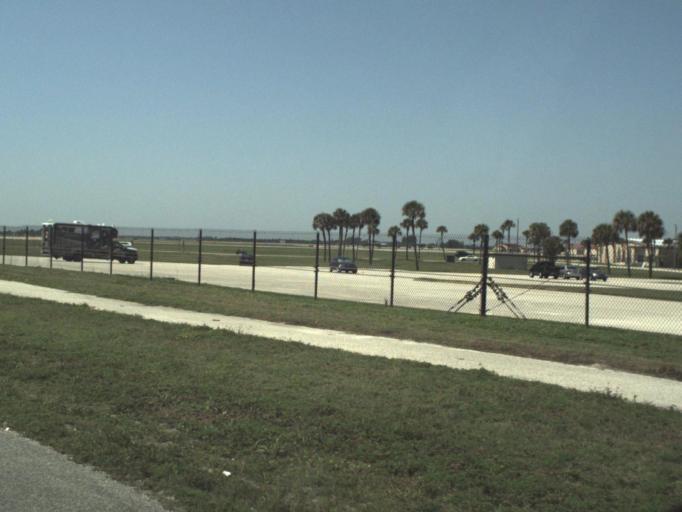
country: US
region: Florida
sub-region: Brevard County
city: South Patrick Shores
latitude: 28.2519
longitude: -80.6036
